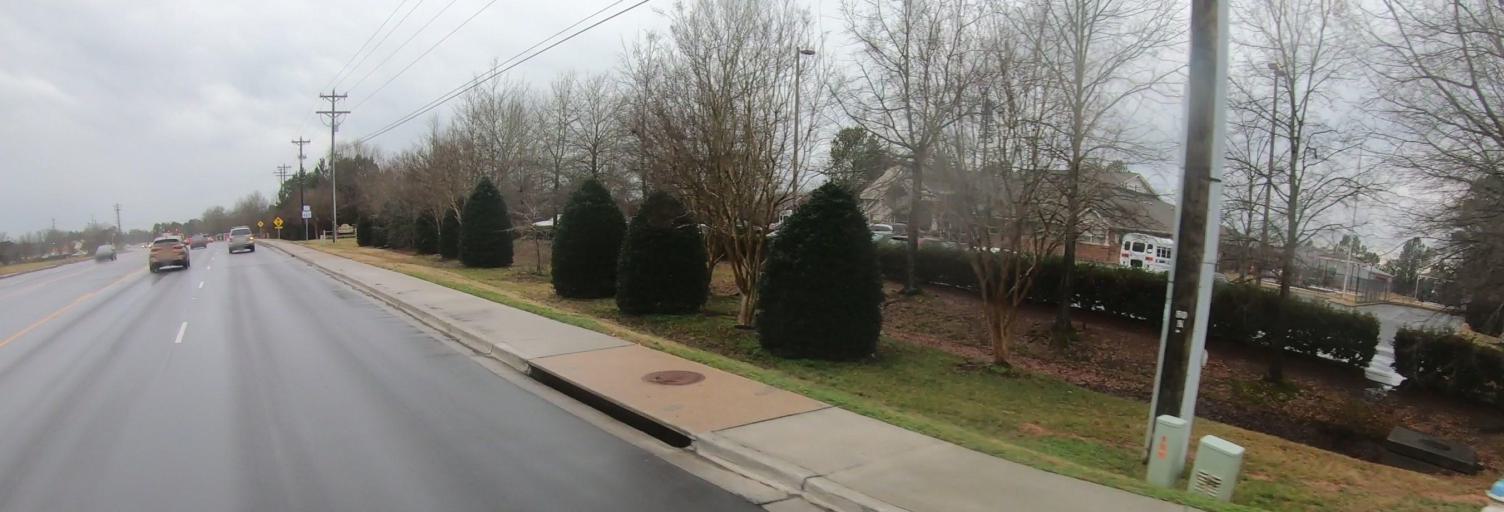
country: US
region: South Carolina
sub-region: York County
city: Tega Cay
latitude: 35.0646
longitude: -80.9911
